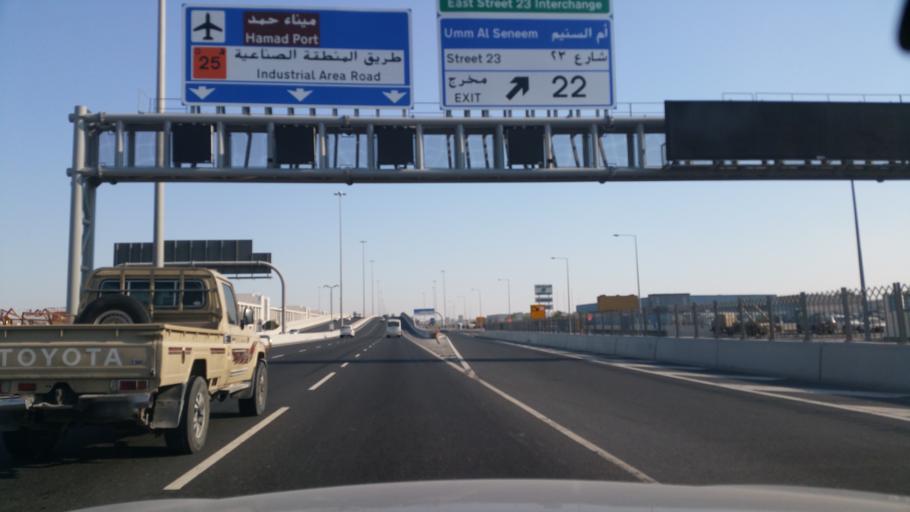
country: QA
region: Baladiyat ar Rayyan
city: Ar Rayyan
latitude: 25.2070
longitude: 51.4449
